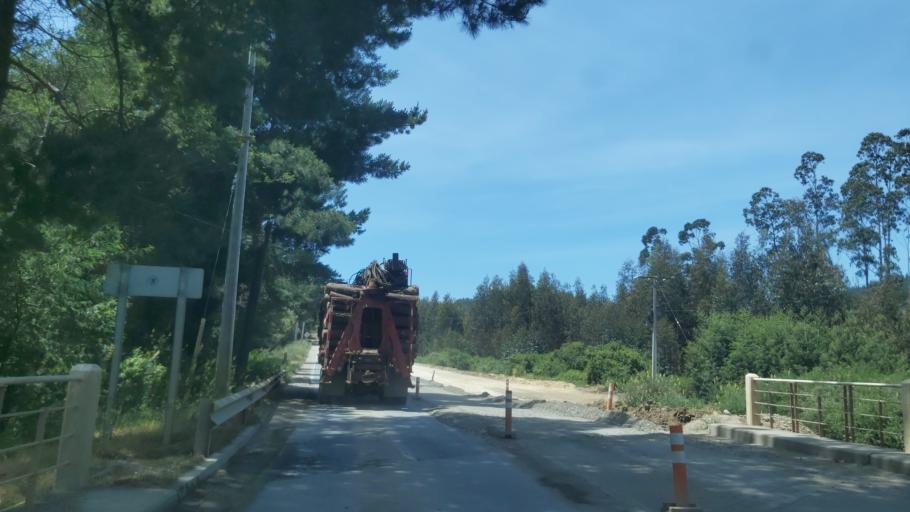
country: CL
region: Maule
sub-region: Provincia de Talca
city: Constitucion
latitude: -35.4477
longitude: -72.4699
